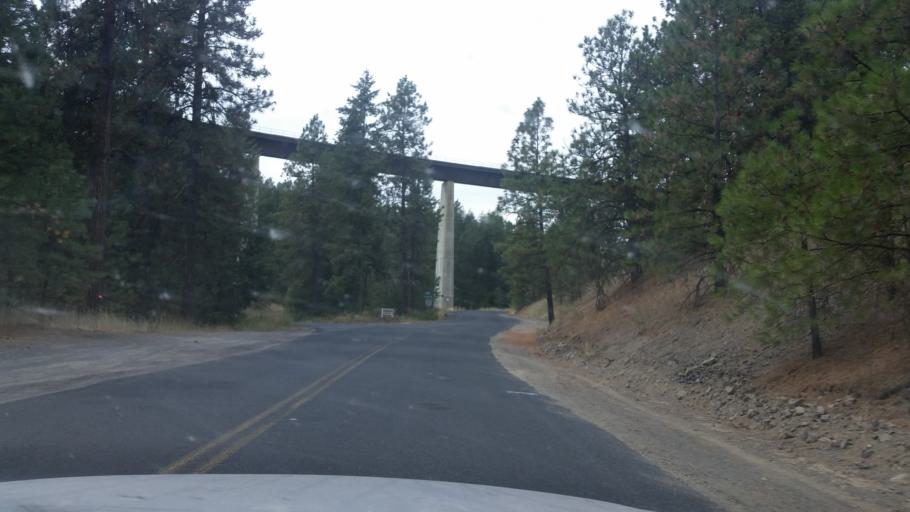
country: US
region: Washington
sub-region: Spokane County
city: Spokane
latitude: 47.6560
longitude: -117.4703
